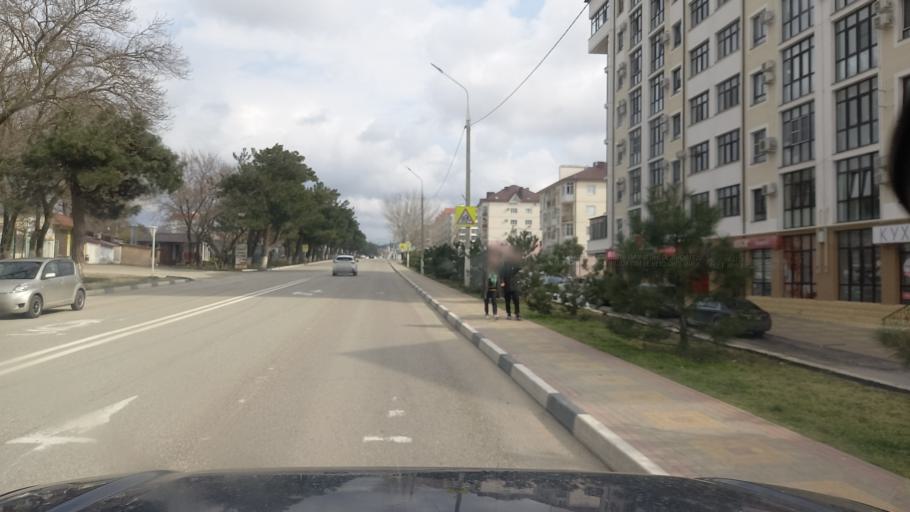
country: RU
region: Krasnodarskiy
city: Gelendzhik
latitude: 44.5587
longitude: 38.0992
